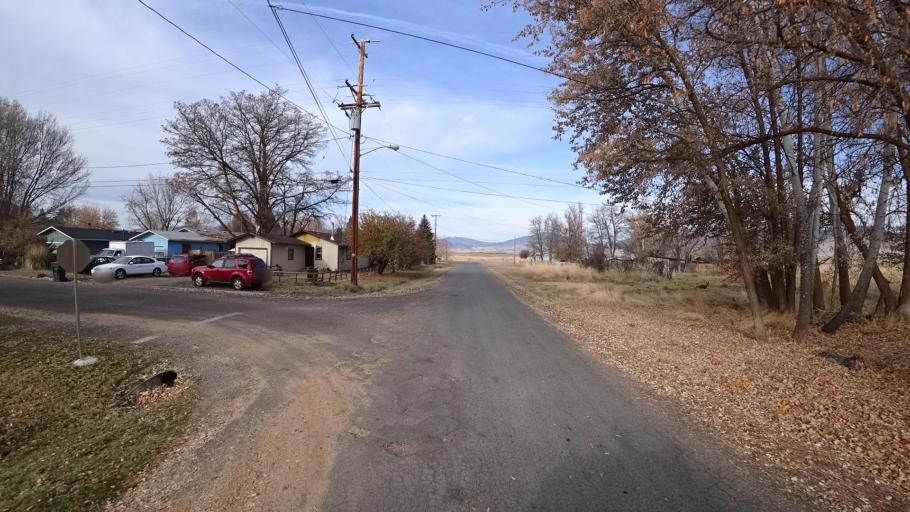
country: US
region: California
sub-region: Siskiyou County
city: Montague
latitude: 41.7325
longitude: -122.5311
